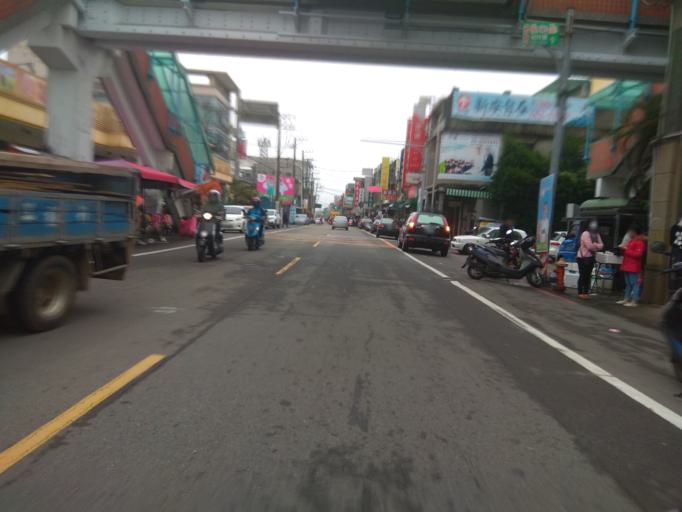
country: TW
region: Taiwan
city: Taoyuan City
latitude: 25.0122
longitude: 121.1373
